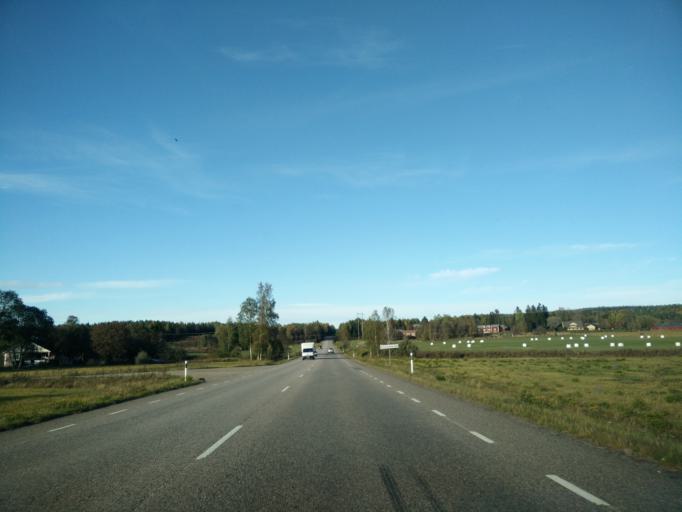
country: SE
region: Gaevleborg
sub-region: Hudiksvalls Kommun
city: Hudiksvall
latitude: 61.7568
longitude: 17.1216
